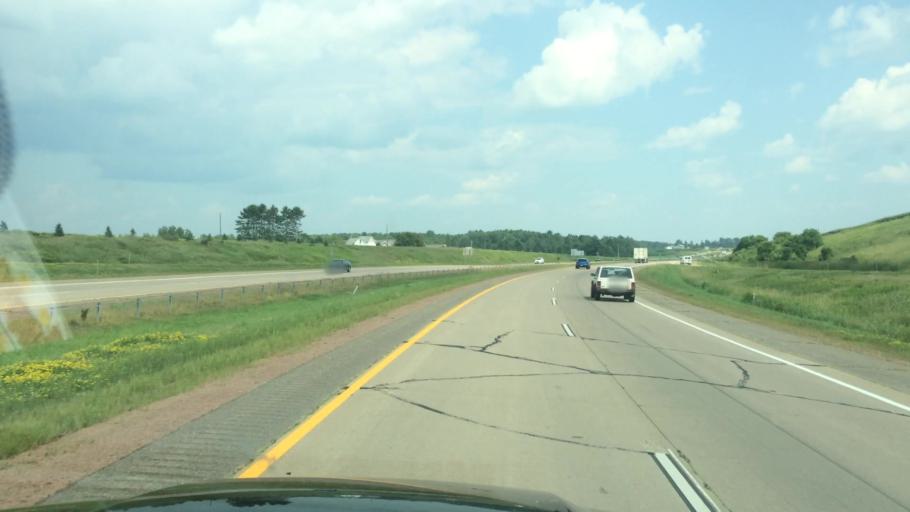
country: US
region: Wisconsin
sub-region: Clark County
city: Abbotsford
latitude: 44.9448
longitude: -90.2878
